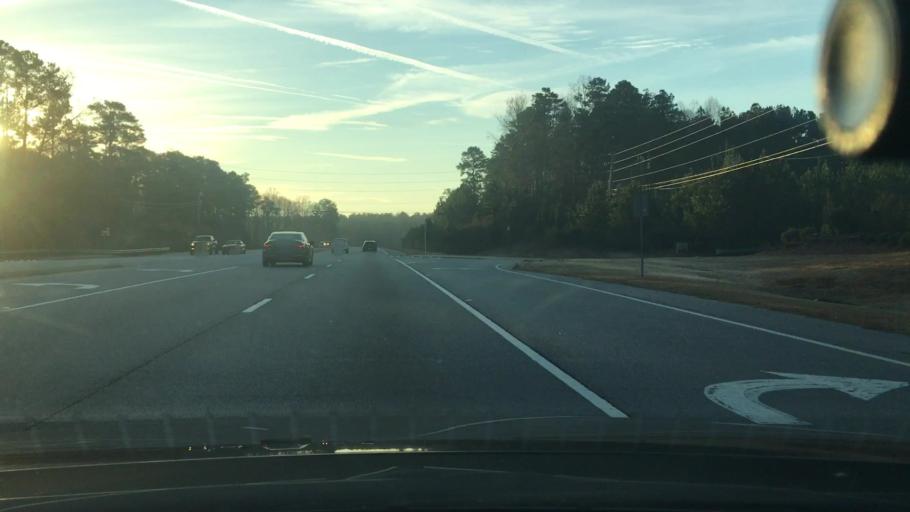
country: US
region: Georgia
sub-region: Fayette County
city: Peachtree City
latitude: 33.3678
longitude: -84.5660
